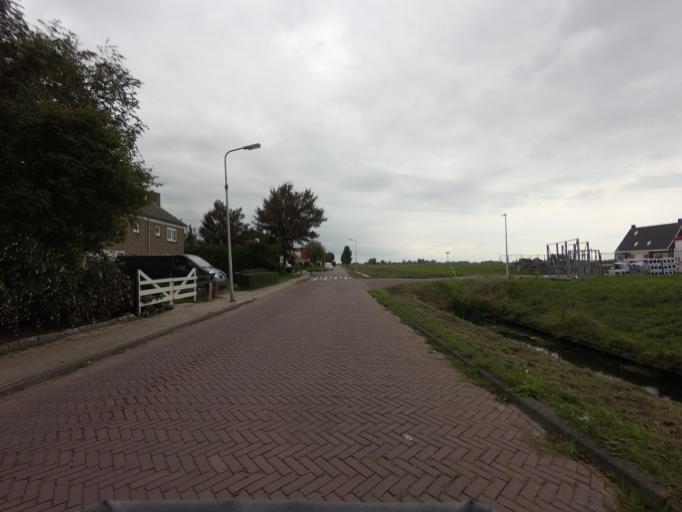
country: NL
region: Friesland
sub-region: Sudwest Fryslan
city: IJlst
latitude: 53.0174
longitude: 5.5989
